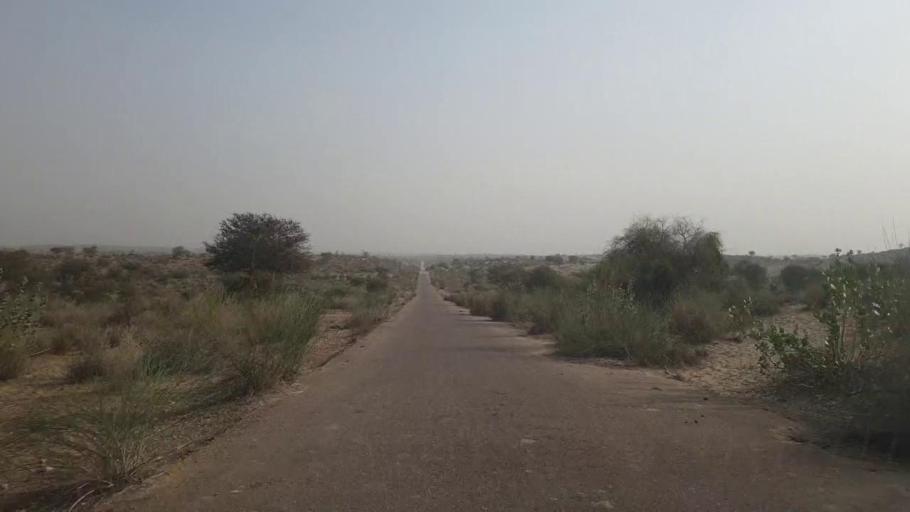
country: PK
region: Sindh
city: Chor
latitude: 25.4465
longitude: 69.9644
